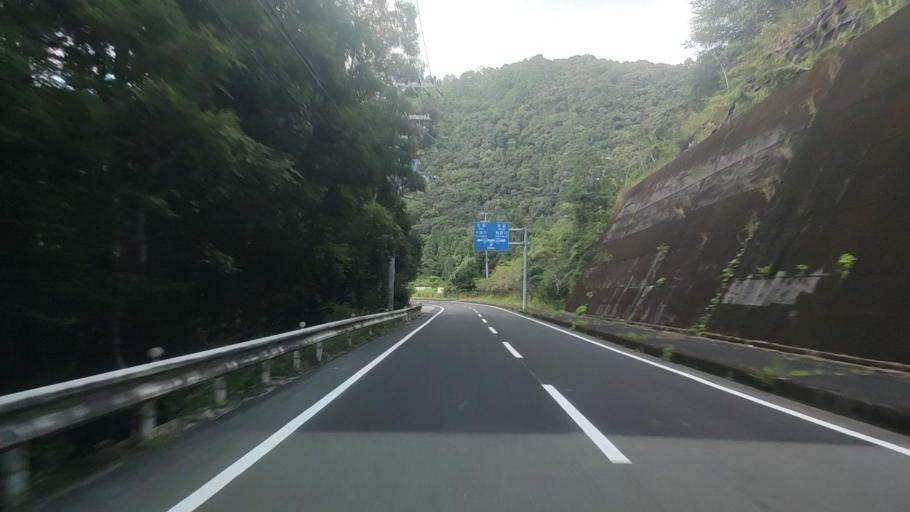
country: JP
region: Wakayama
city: Shingu
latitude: 33.8223
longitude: 135.7752
